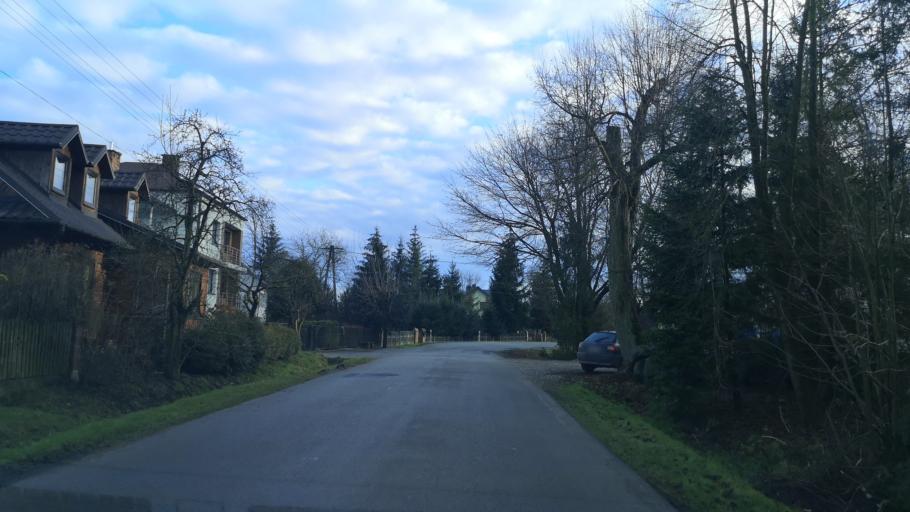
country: PL
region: Subcarpathian Voivodeship
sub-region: Powiat lezajski
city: Piskorowice
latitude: 50.2600
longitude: 22.5968
